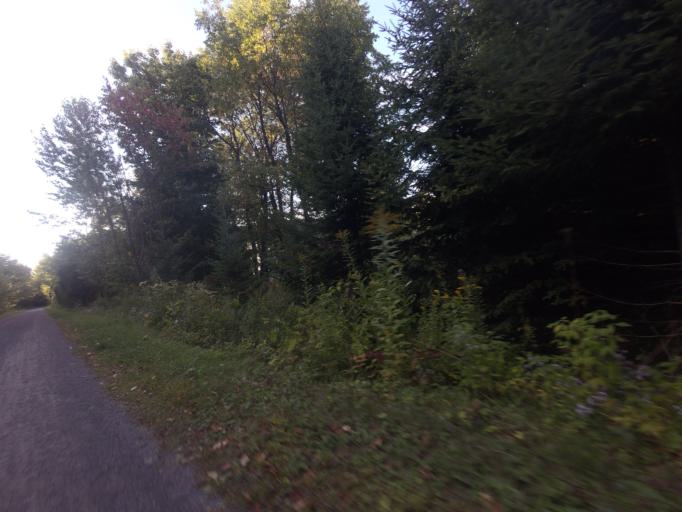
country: CA
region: Quebec
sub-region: Laurentides
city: Saint-Jerome
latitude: 45.8107
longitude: -74.0370
